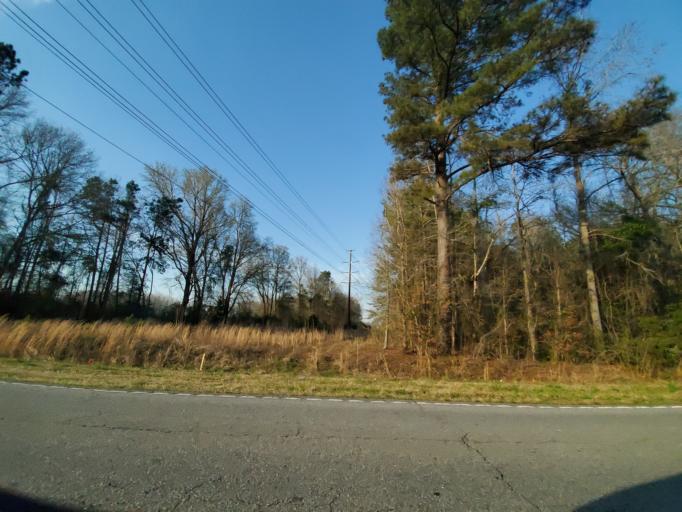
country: US
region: South Carolina
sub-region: Bamberg County
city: Bamberg
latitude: 33.3039
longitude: -81.0611
